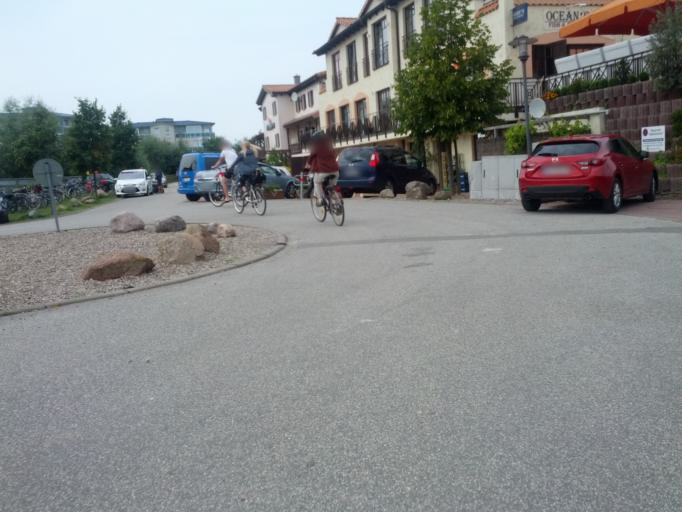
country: DE
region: Mecklenburg-Vorpommern
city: Ostseebad Kuhlungsborn
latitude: 54.1514
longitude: 11.7695
